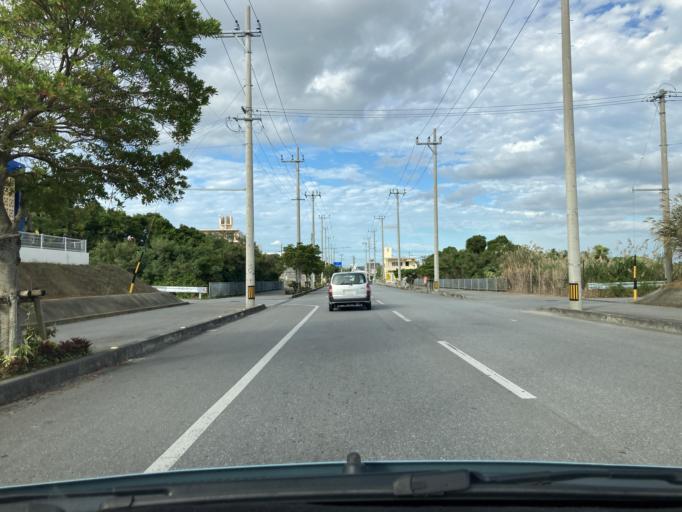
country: JP
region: Okinawa
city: Gushikawa
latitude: 26.3711
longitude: 127.8267
